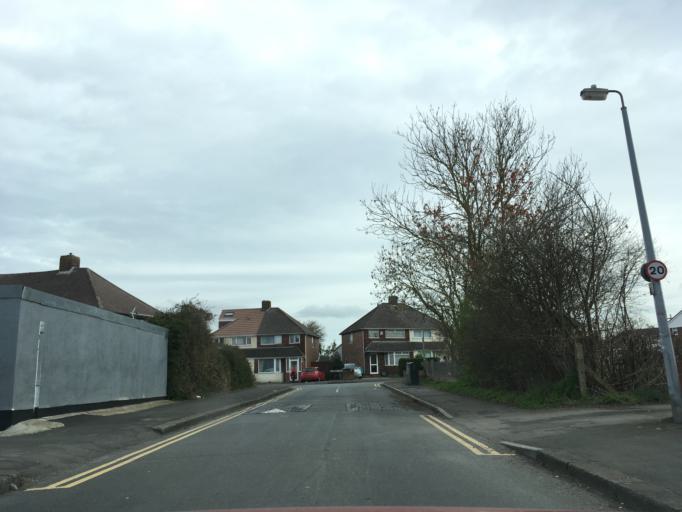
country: GB
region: England
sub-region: South Gloucestershire
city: Almondsbury
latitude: 51.5324
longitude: -2.5829
